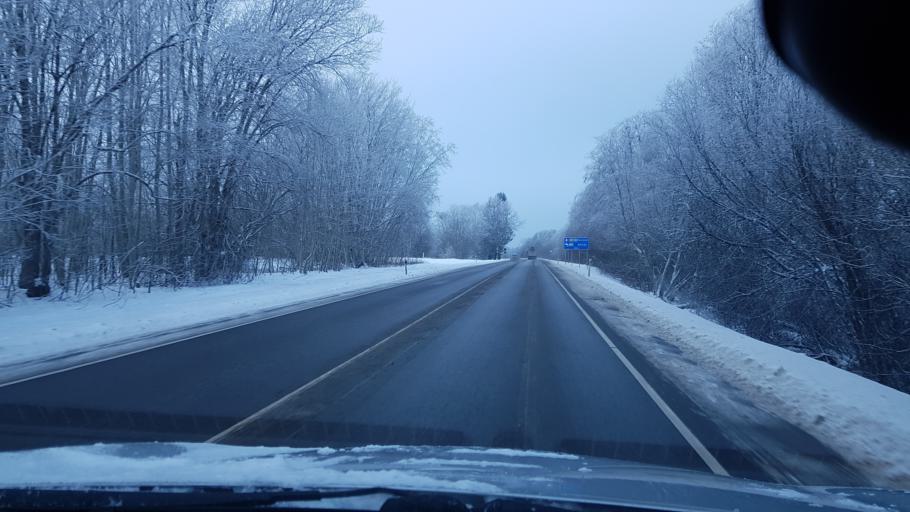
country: EE
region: Harju
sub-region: Paldiski linn
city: Paldiski
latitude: 59.3405
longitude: 24.2007
